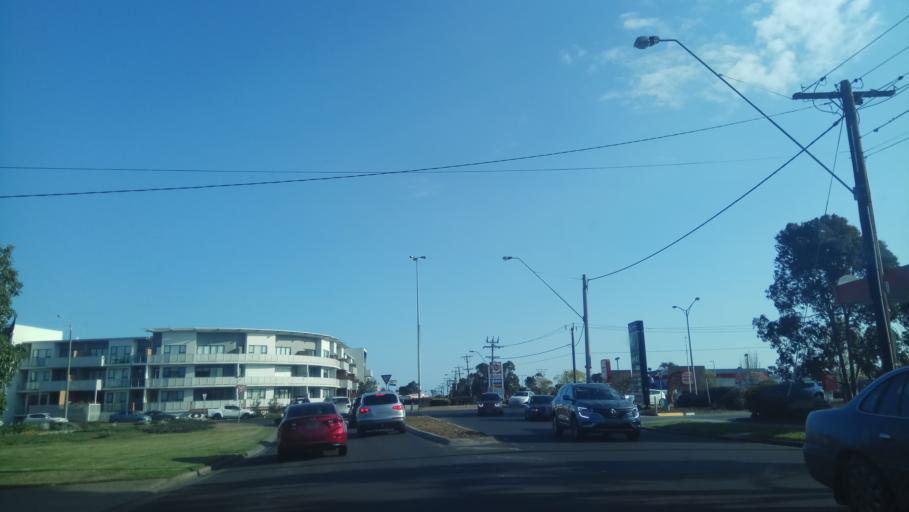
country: AU
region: Victoria
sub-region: Hobsons Bay
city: Laverton
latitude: -37.8709
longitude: 144.7777
